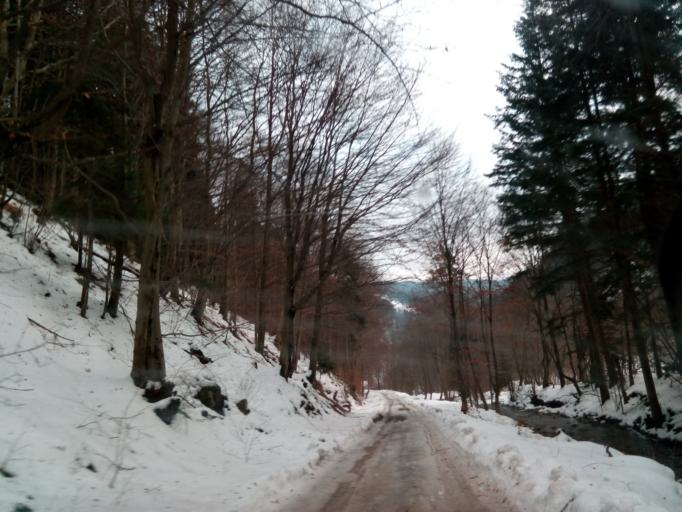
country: SK
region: Presovsky
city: Sabinov
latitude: 49.2000
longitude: 21.0844
